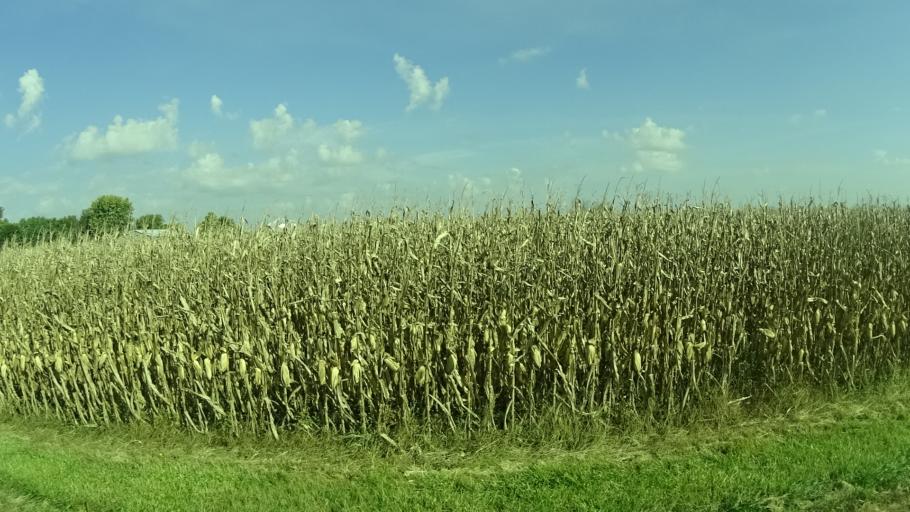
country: US
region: Indiana
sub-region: Madison County
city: Lapel
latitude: 40.0315
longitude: -85.8415
